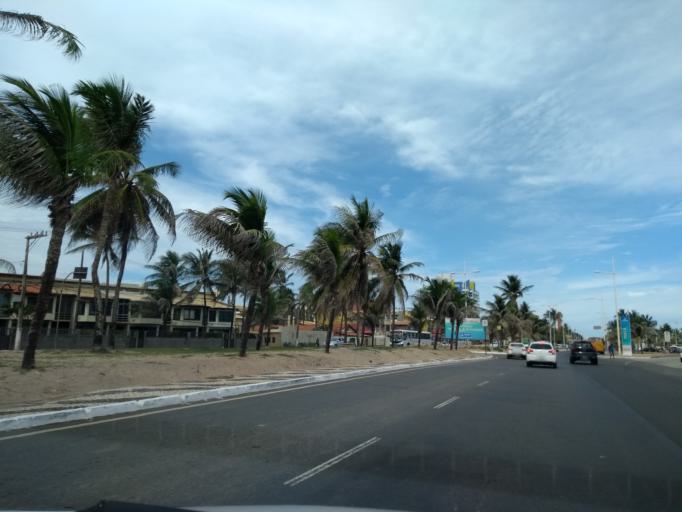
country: BR
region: Bahia
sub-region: Lauro De Freitas
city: Lauro de Freitas
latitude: -12.9547
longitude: -38.3841
